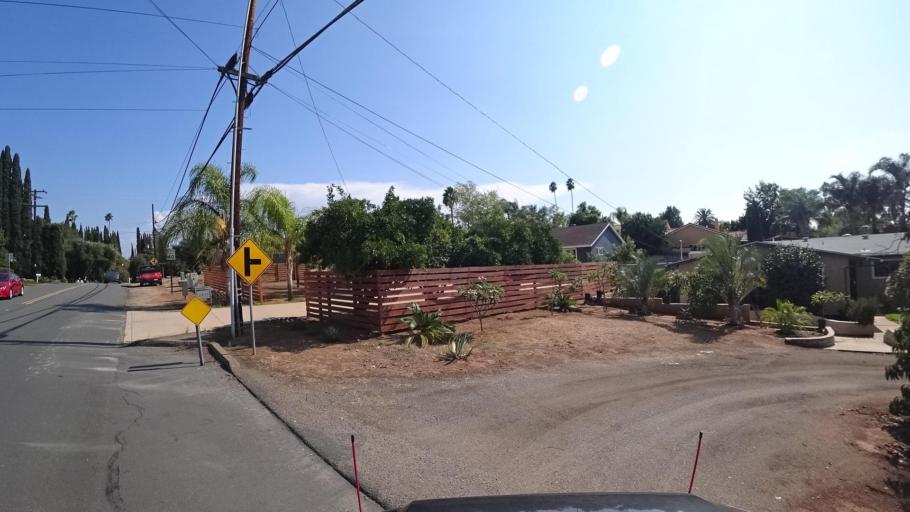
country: US
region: California
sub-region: San Diego County
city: Escondido
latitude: 33.0999
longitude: -117.0680
